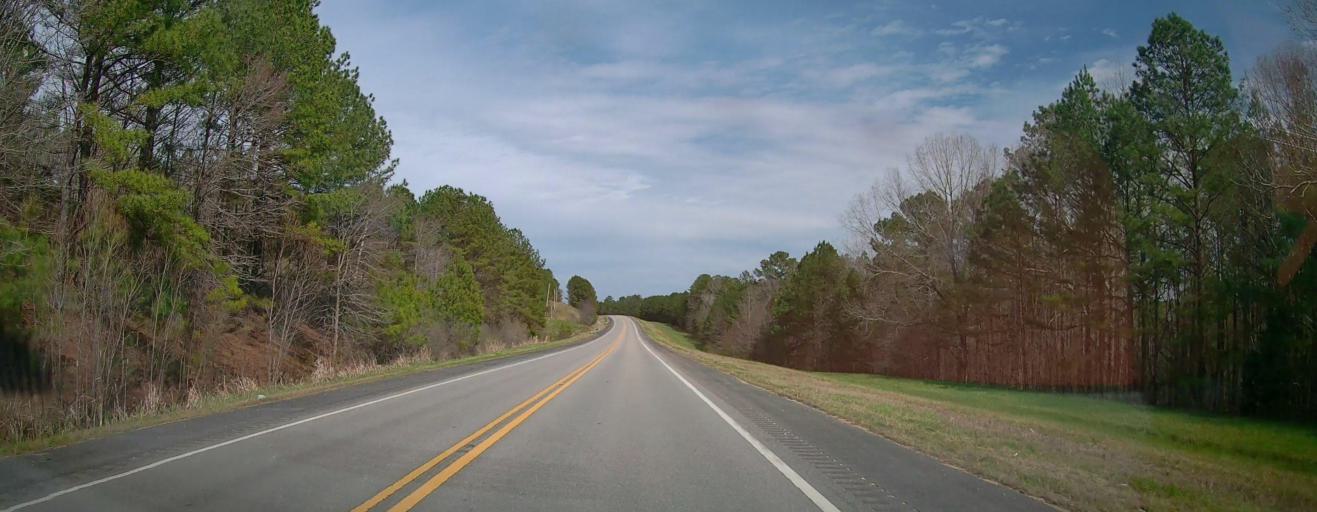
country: US
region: Alabama
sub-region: Marion County
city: Winfield
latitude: 33.9297
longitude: -87.6706
